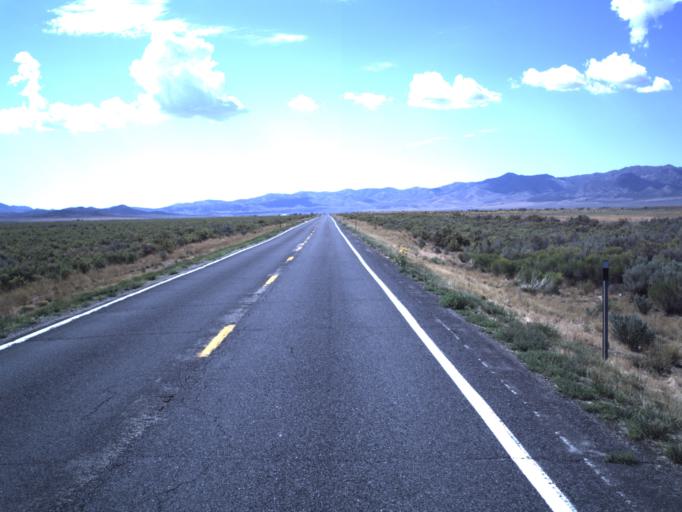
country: US
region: Utah
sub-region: Tooele County
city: Tooele
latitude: 40.1467
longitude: -112.4308
